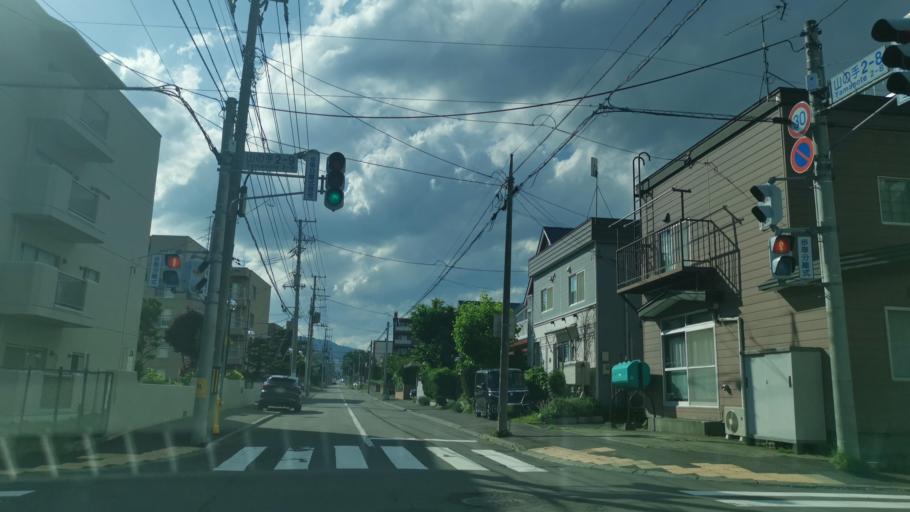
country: JP
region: Hokkaido
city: Sapporo
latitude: 43.0646
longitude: 141.2963
